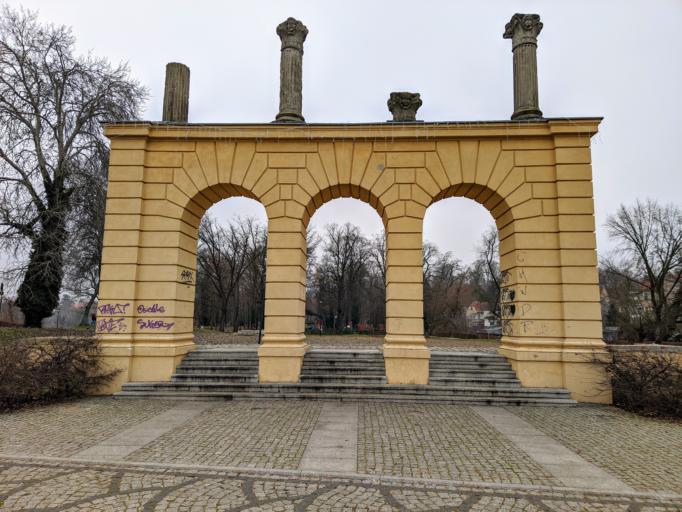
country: DE
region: Brandenburg
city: Guben
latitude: 51.9536
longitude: 14.7209
